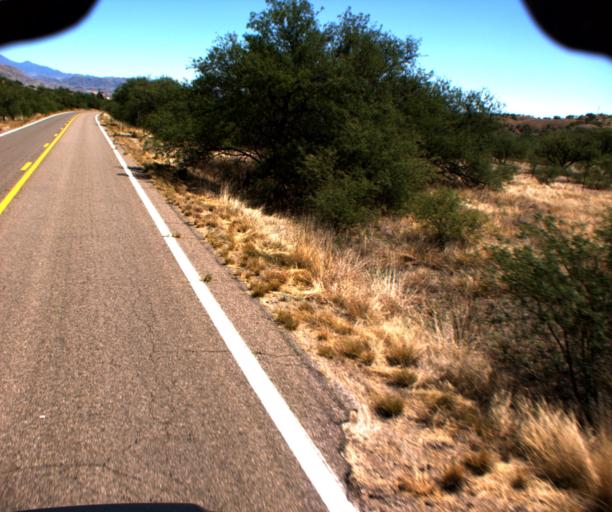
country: US
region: Arizona
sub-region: Santa Cruz County
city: Rio Rico
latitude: 31.4264
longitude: -111.0086
